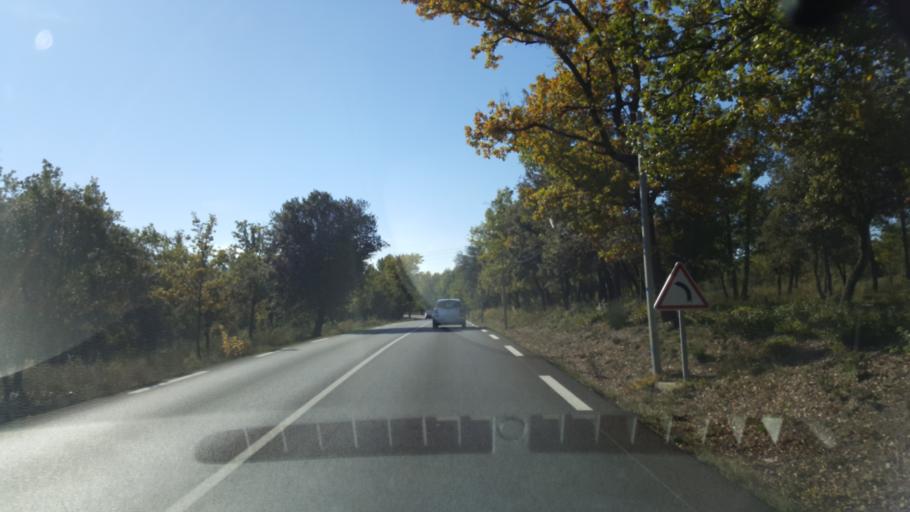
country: FR
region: Provence-Alpes-Cote d'Azur
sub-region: Departement du Var
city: Rougiers
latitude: 43.4168
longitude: 5.8295
